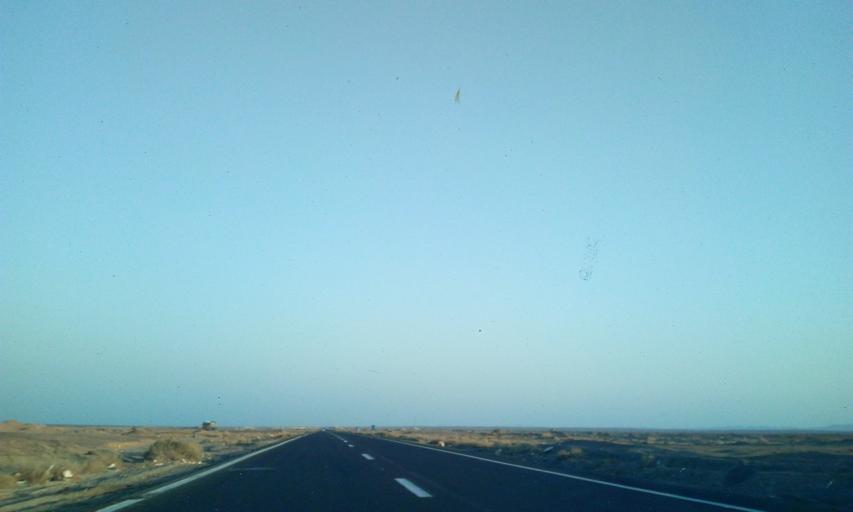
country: EG
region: South Sinai
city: Tor
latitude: 27.8489
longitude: 33.4361
